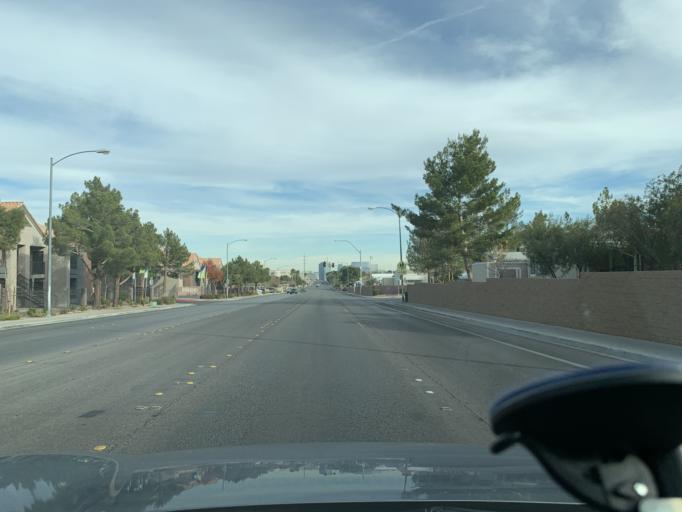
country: US
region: Nevada
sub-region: Clark County
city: Spring Valley
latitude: 36.1073
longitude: -115.2224
